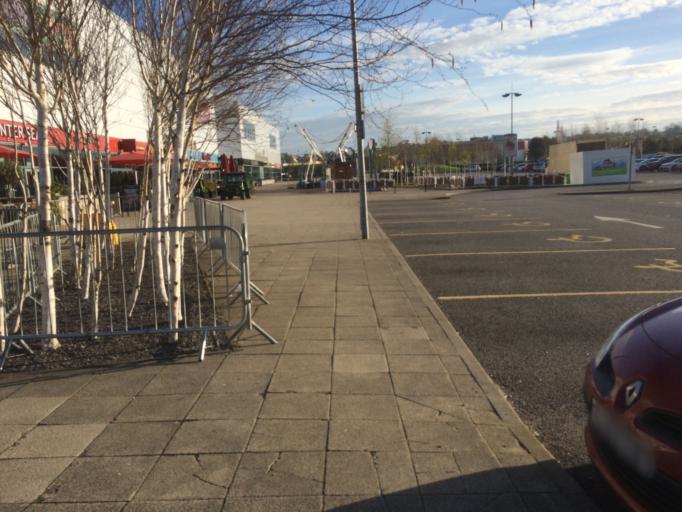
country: GB
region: England
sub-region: City and Borough of Wakefield
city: Castleford
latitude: 53.7093
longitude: -1.3407
